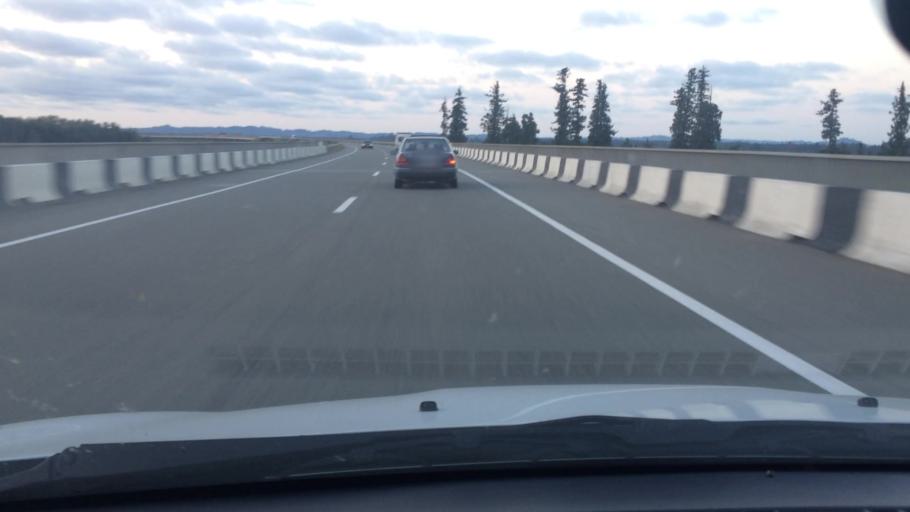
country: GE
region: Ajaria
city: Ochkhamuri
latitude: 41.8599
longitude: 41.8382
